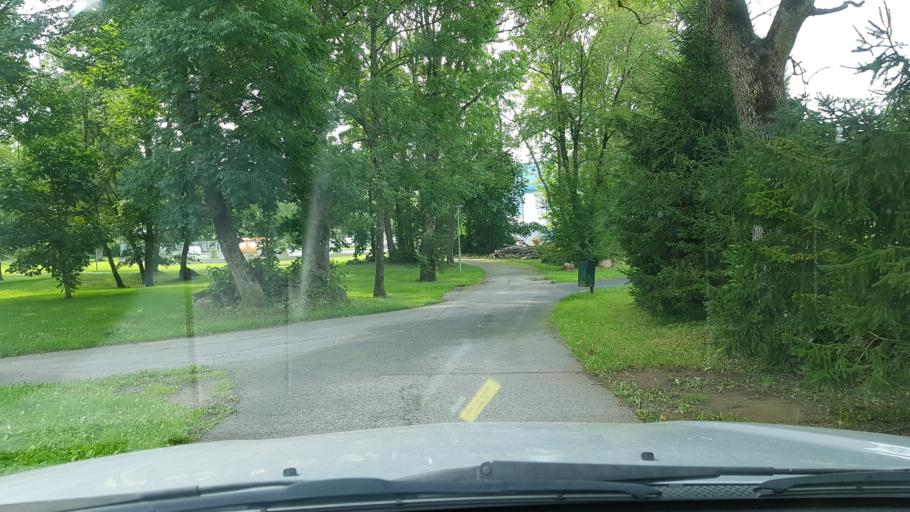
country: EE
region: Harju
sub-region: Rae vald
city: Jueri
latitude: 59.3581
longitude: 24.9211
